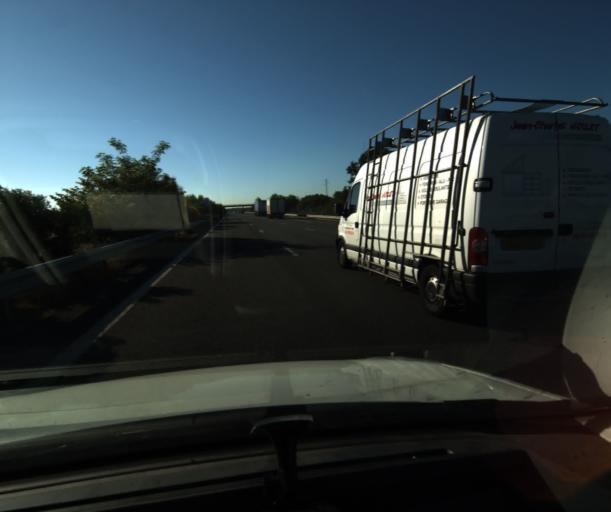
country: FR
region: Midi-Pyrenees
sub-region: Departement du Tarn-et-Garonne
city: Pompignan
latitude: 43.8413
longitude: 1.3281
